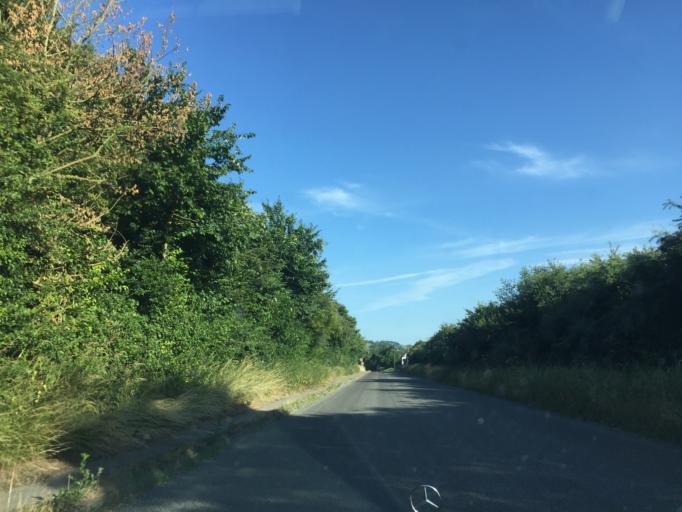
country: GB
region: England
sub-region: Oxfordshire
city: Thame
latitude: 51.6930
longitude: -0.9790
